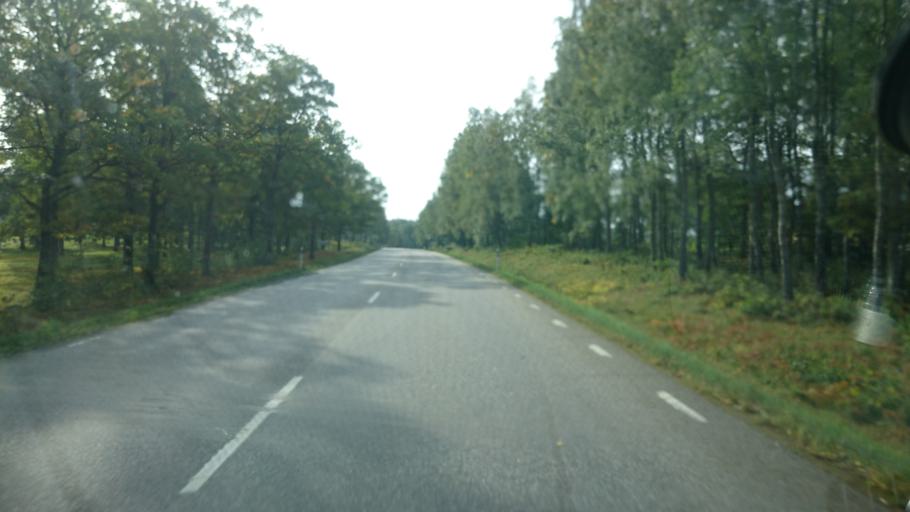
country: SE
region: Vaestra Goetaland
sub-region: Alingsas Kommun
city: Sollebrunn
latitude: 58.0737
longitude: 12.4820
